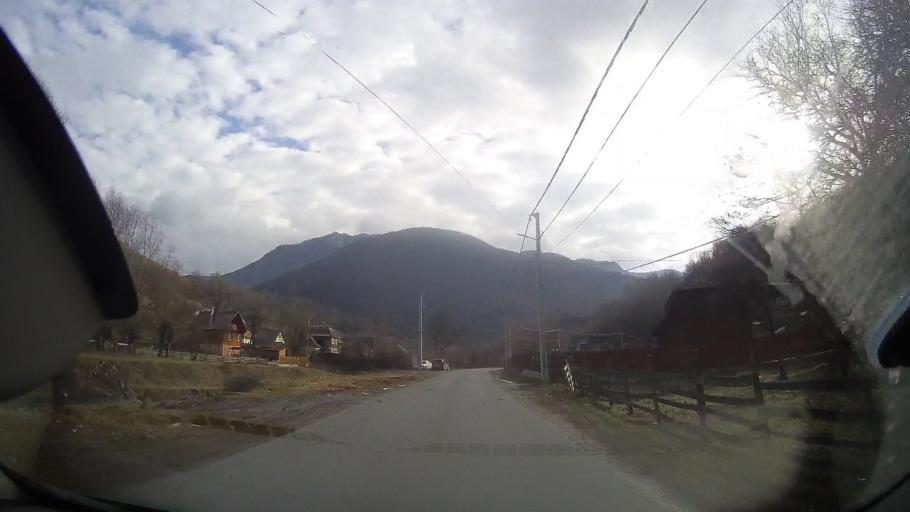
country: RO
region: Alba
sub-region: Comuna Ocolis
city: Ocolis
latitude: 46.4736
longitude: 23.4714
